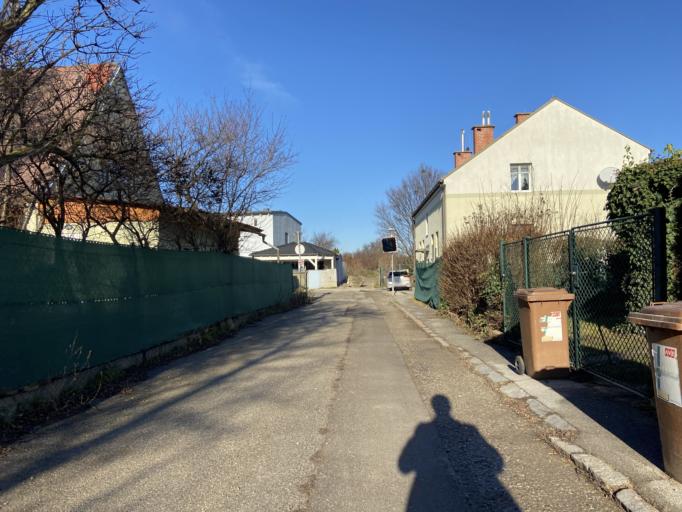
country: AT
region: Lower Austria
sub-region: Politischer Bezirk Modling
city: Neu-Guntramsdorf
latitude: 48.0656
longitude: 16.3243
